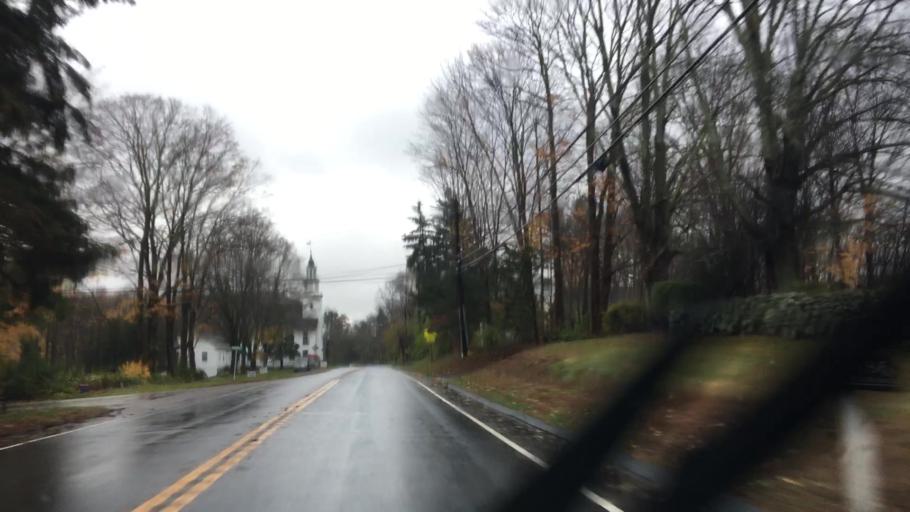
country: US
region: Connecticut
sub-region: New Haven County
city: Oxford
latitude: 41.4281
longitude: -73.1564
